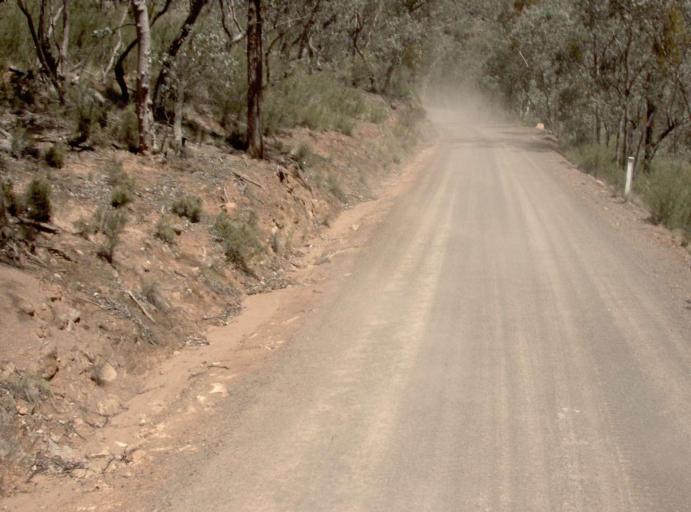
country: AU
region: New South Wales
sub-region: Snowy River
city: Jindabyne
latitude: -37.0635
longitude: 148.5042
